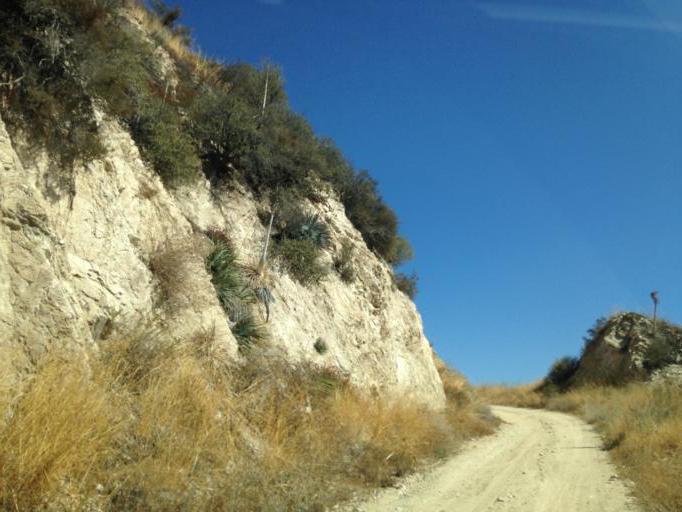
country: US
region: California
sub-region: San Bernardino County
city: Running Springs
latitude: 34.1378
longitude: -117.0986
